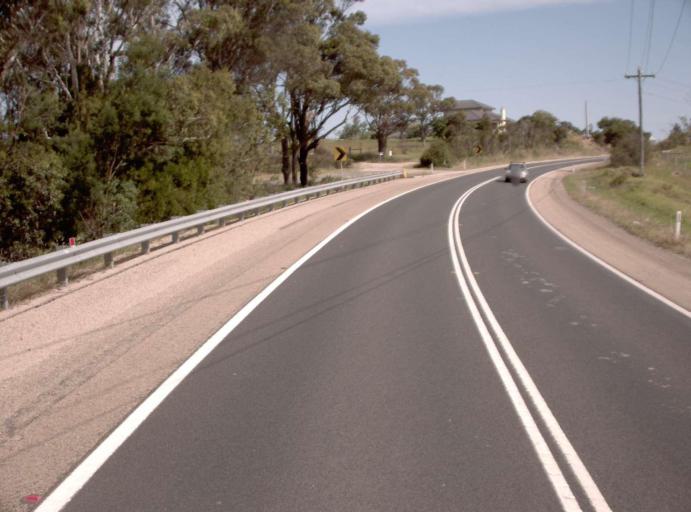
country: AU
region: Victoria
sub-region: East Gippsland
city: Lakes Entrance
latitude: -37.8611
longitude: 147.9524
